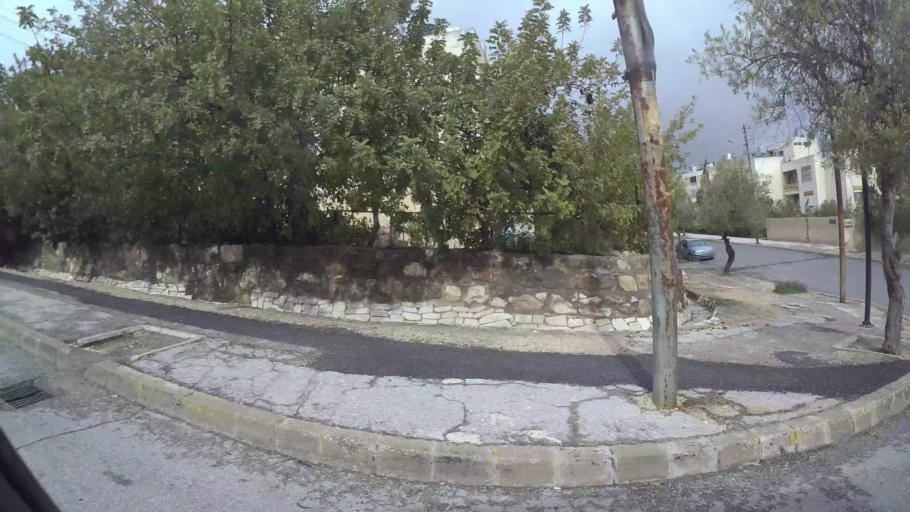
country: JO
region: Amman
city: Al Jubayhah
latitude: 32.0532
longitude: 35.8827
